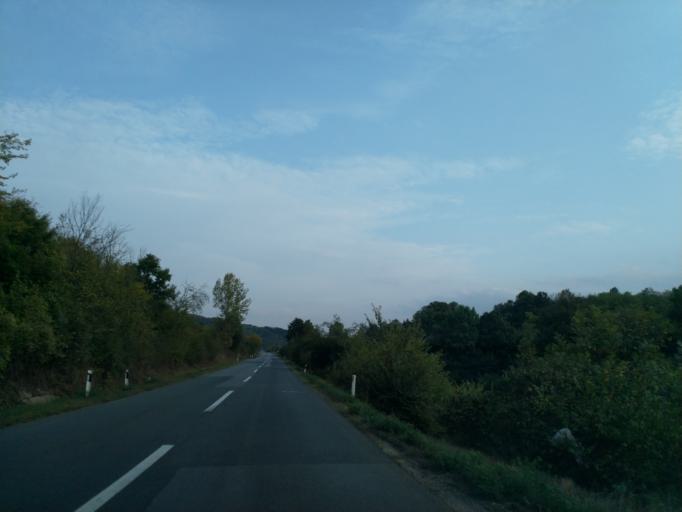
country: RS
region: Central Serbia
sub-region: Sumadijski Okrug
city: Topola
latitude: 44.2268
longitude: 20.7129
